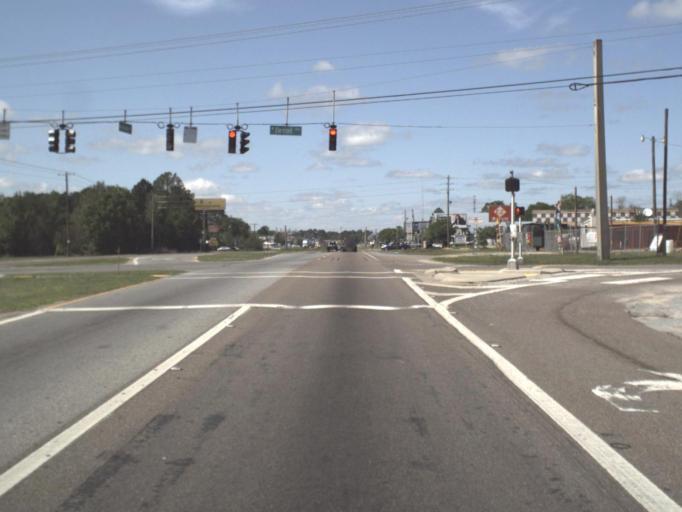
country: US
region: Florida
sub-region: Escambia County
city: Ensley
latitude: 30.5185
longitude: -87.2725
